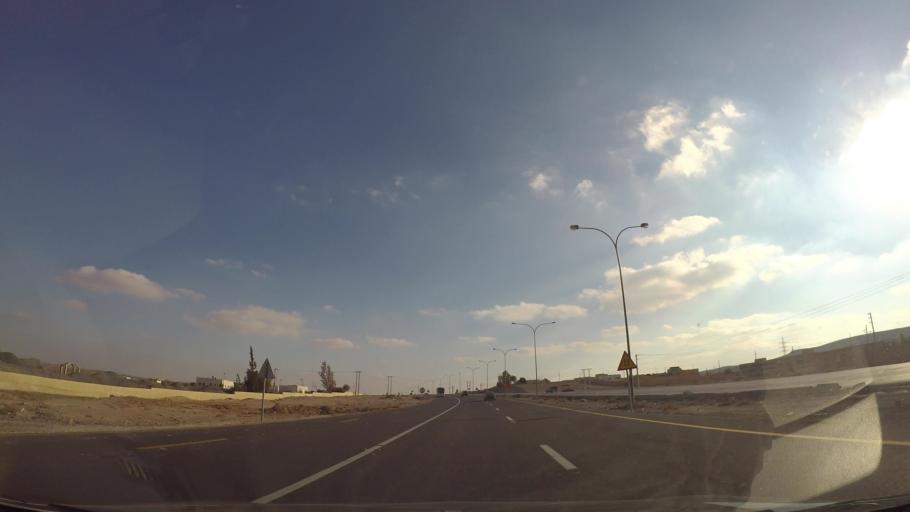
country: JO
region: Karak
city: Karak City
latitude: 31.0869
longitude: 36.0070
